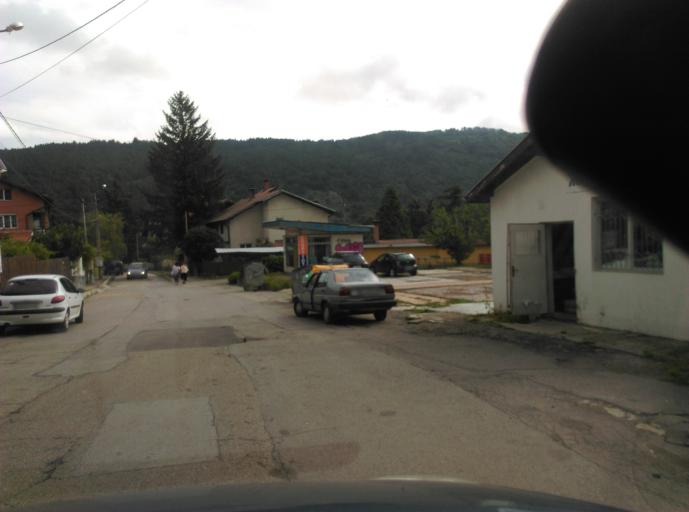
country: BG
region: Sofia-Capital
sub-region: Stolichna Obshtina
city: Sofia
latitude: 42.5934
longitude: 23.4112
